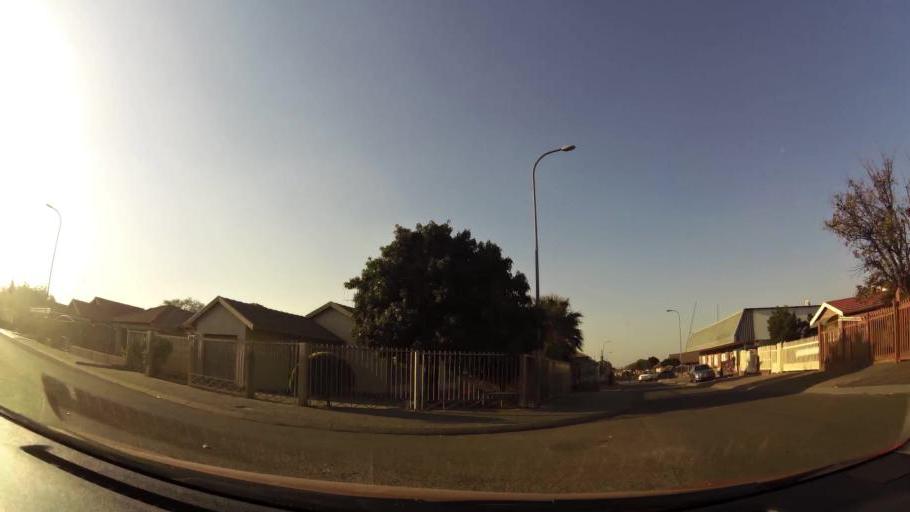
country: ZA
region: North-West
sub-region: Bojanala Platinum District Municipality
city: Rustenburg
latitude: -25.6473
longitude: 27.2229
